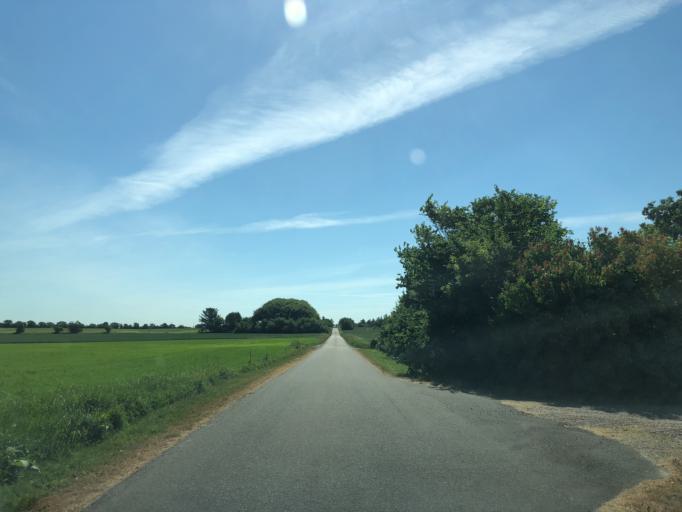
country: DK
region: Central Jutland
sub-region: Struer Kommune
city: Struer
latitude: 56.4328
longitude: 8.4512
